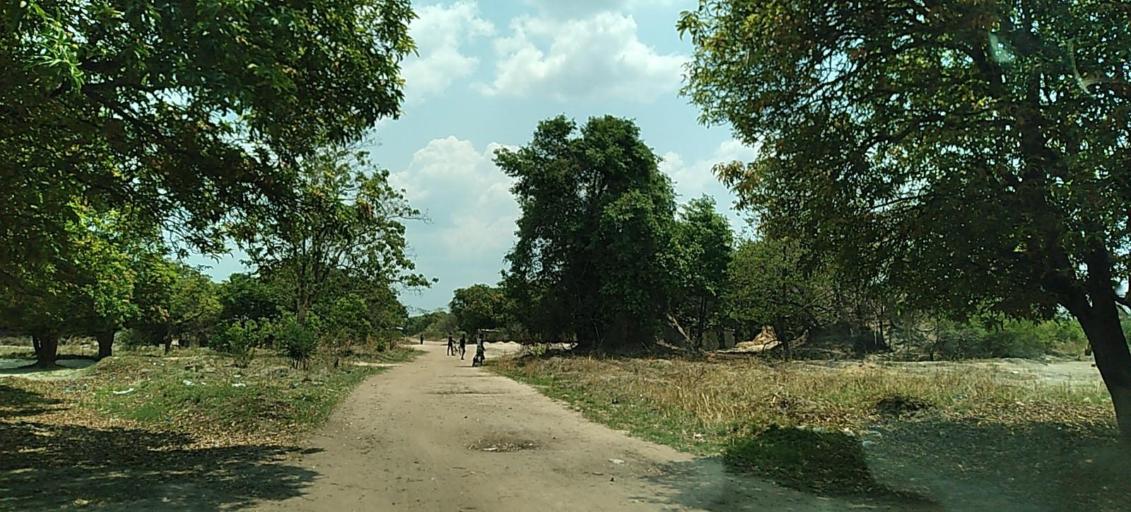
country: ZM
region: Copperbelt
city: Luanshya
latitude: -13.1559
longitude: 28.3132
